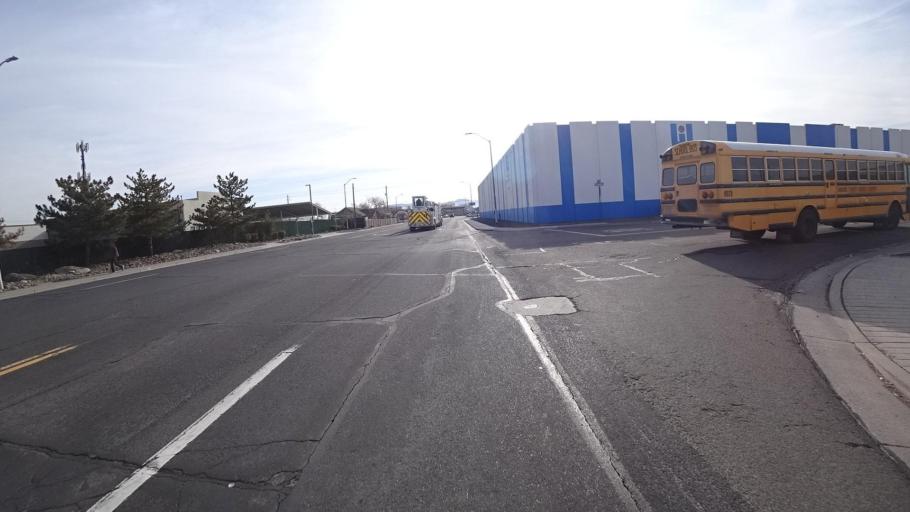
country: US
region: Nevada
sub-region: Washoe County
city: Reno
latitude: 39.5346
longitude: -119.7969
